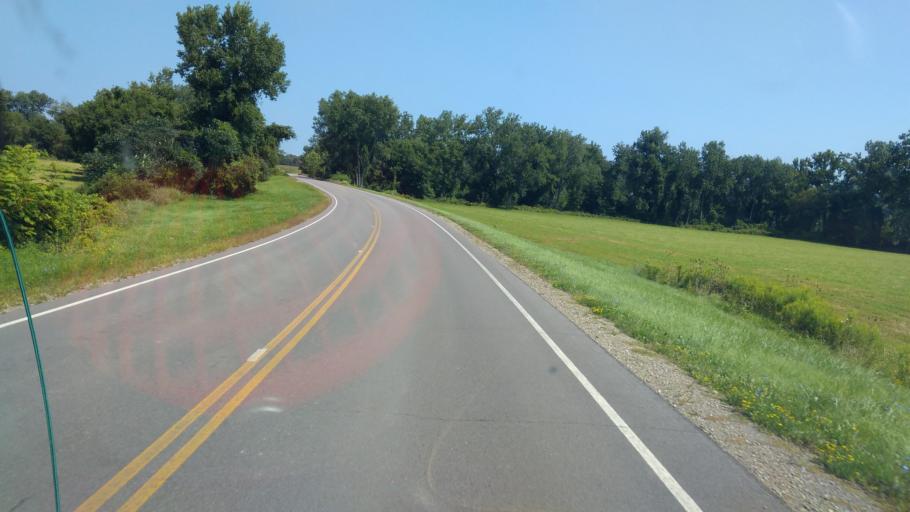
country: US
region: New York
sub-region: Allegany County
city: Belmont
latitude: 42.2612
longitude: -78.0525
